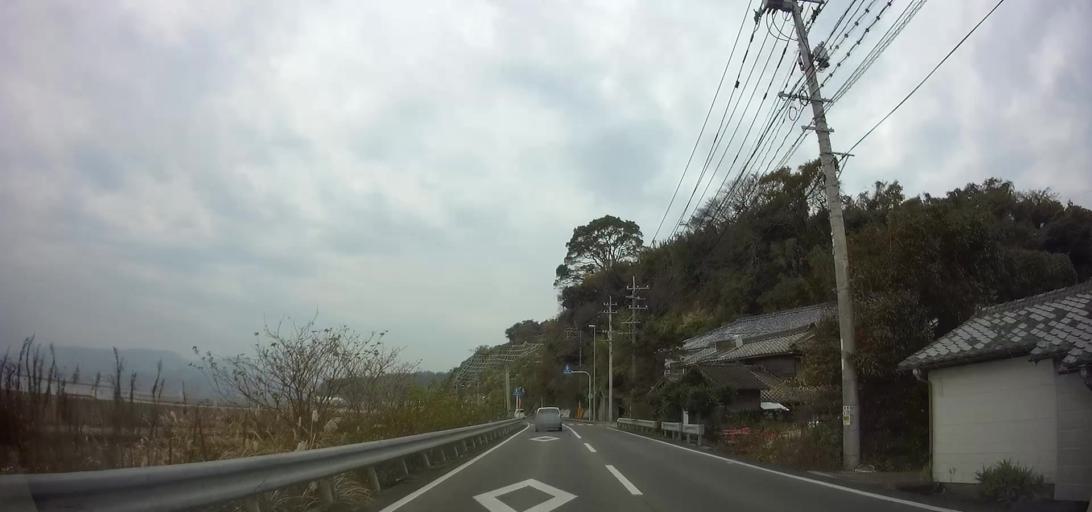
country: JP
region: Nagasaki
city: Shimabara
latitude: 32.6539
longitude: 130.2774
